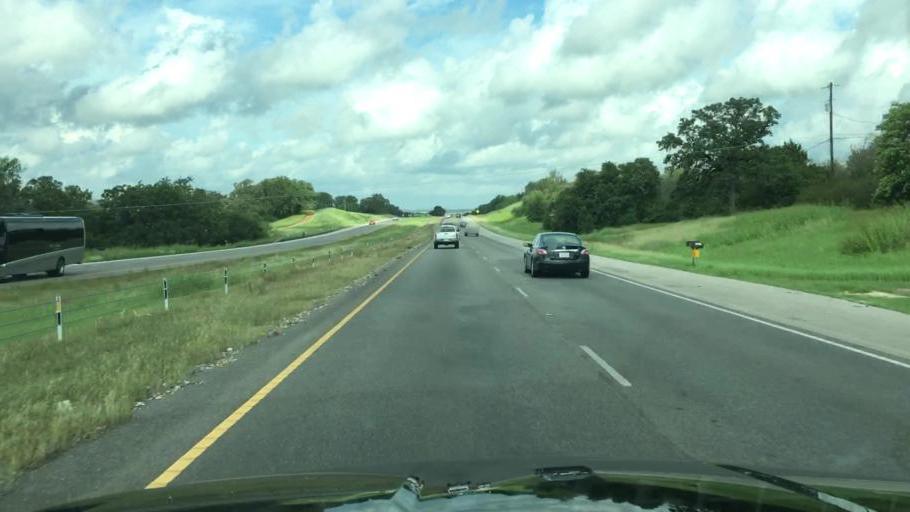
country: US
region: Texas
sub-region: Bastrop County
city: Wyldwood
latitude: 30.1491
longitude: -97.4851
